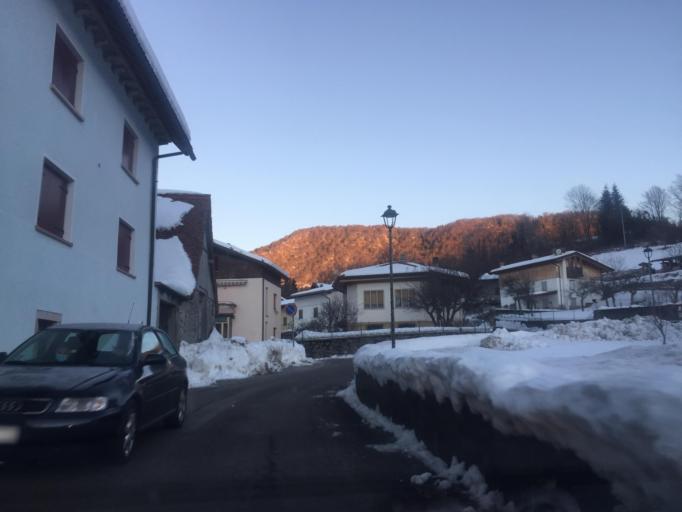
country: IT
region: Friuli Venezia Giulia
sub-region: Provincia di Udine
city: Lauco
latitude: 46.4256
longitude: 12.9321
